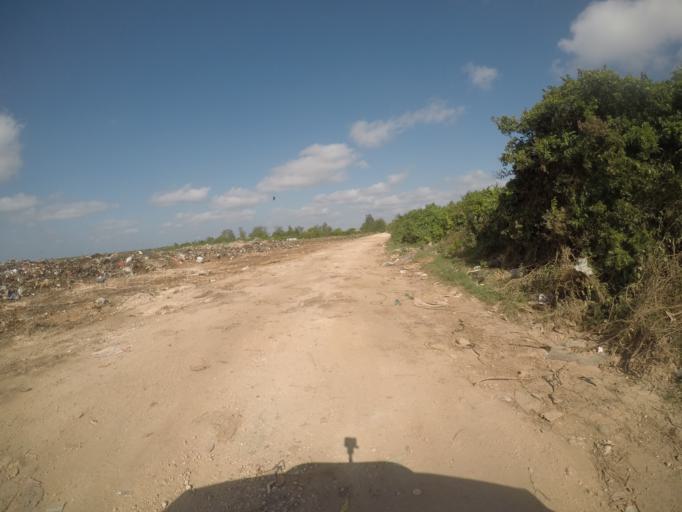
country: TZ
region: Zanzibar Central/South
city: Koani
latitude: -6.2184
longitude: 39.3293
